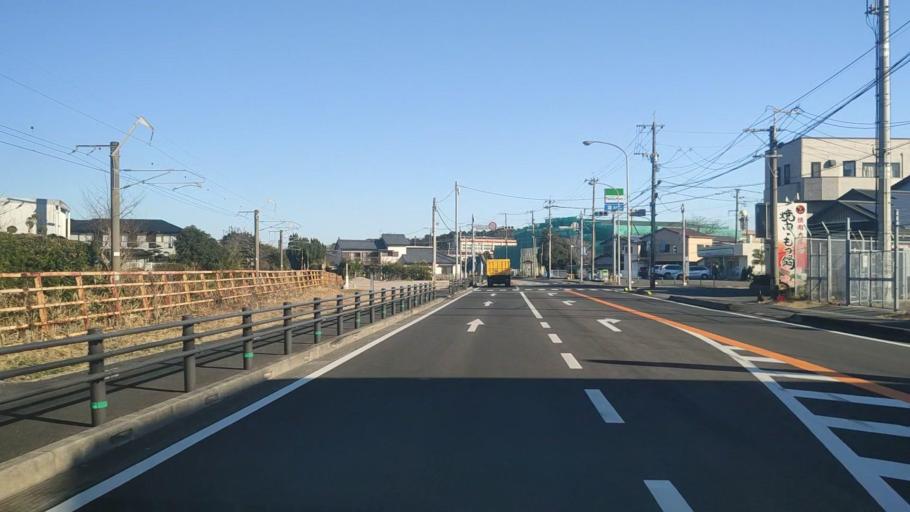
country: JP
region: Miyazaki
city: Nobeoka
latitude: 32.5192
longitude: 131.6829
